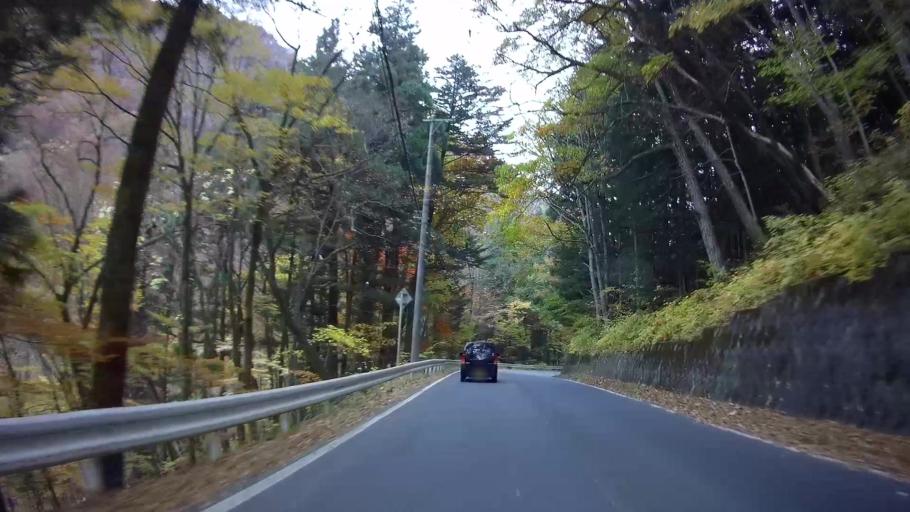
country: JP
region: Gunma
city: Nakanojomachi
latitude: 36.6201
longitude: 138.6448
